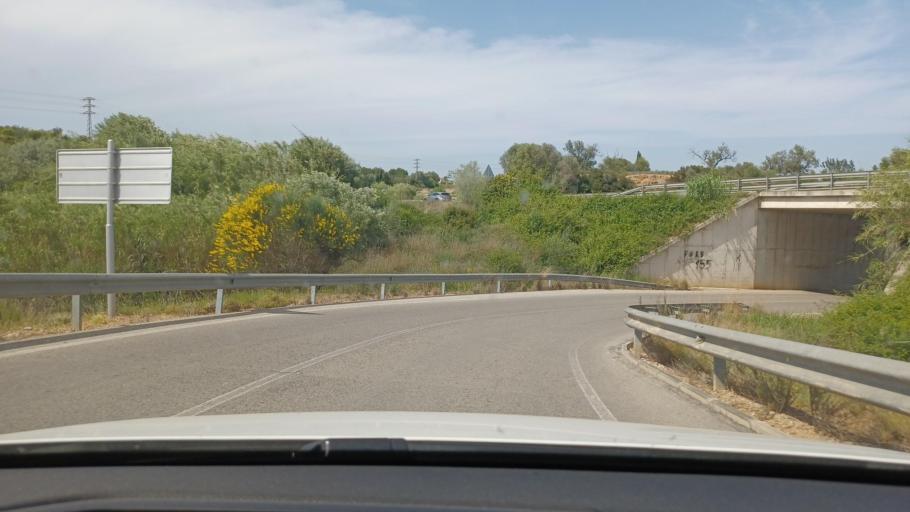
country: ES
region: Catalonia
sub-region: Provincia de Tarragona
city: Amposta
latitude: 40.7115
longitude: 0.5652
